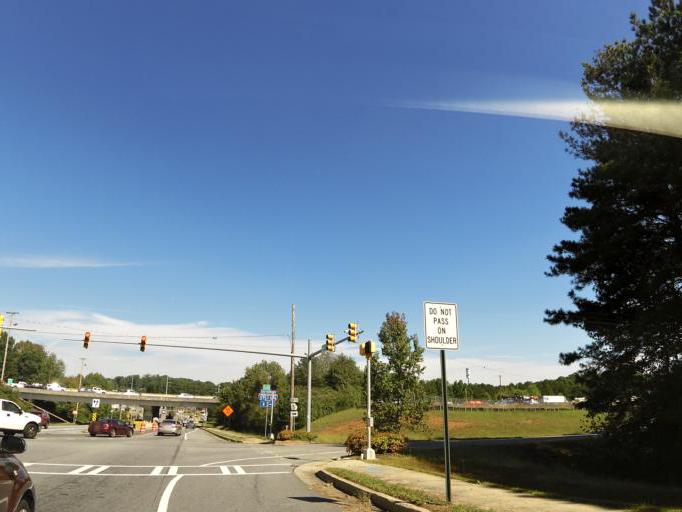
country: US
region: Georgia
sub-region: Cherokee County
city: Woodstock
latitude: 34.0509
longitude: -84.5561
